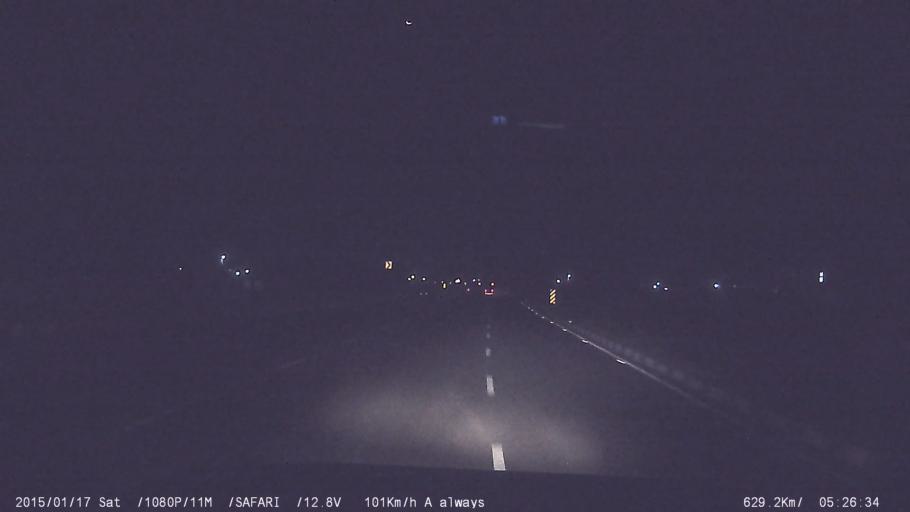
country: IN
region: Tamil Nadu
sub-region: Vellore
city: Arcot
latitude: 12.9381
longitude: 79.2487
